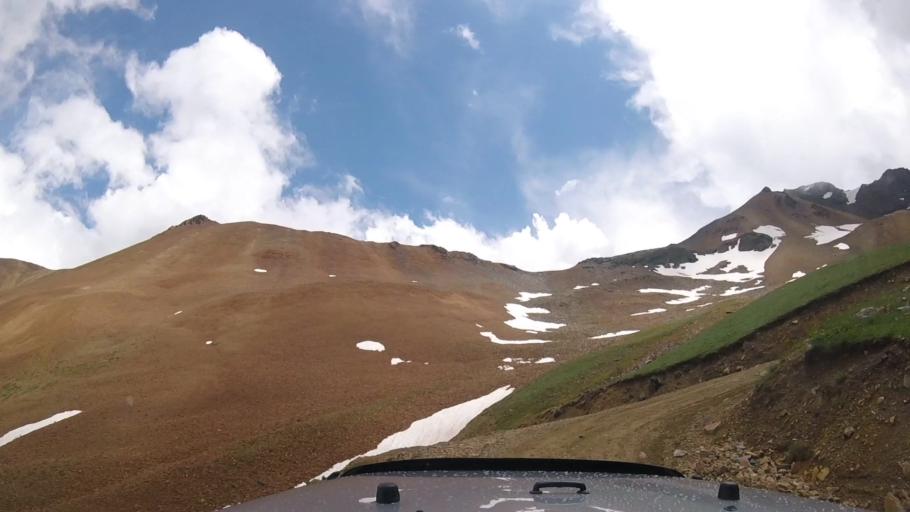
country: US
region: Colorado
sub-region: San Juan County
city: Silverton
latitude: 37.9161
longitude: -107.6120
